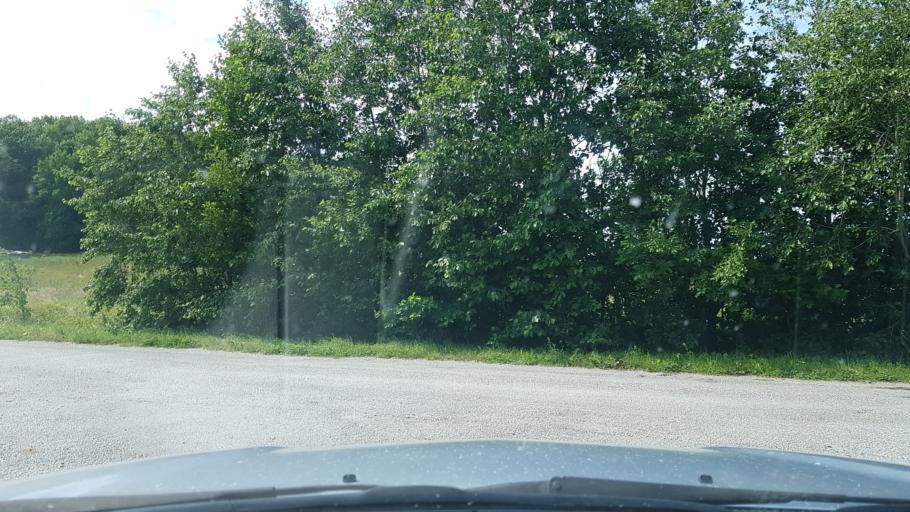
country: EE
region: Ida-Virumaa
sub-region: Sillamaee linn
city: Sillamae
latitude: 59.3757
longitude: 27.8703
